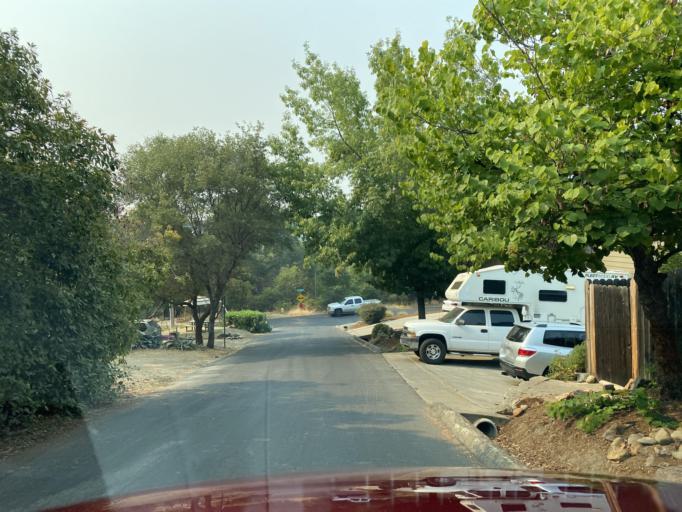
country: US
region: California
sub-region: Sacramento County
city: Folsom
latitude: 38.6804
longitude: -121.1728
